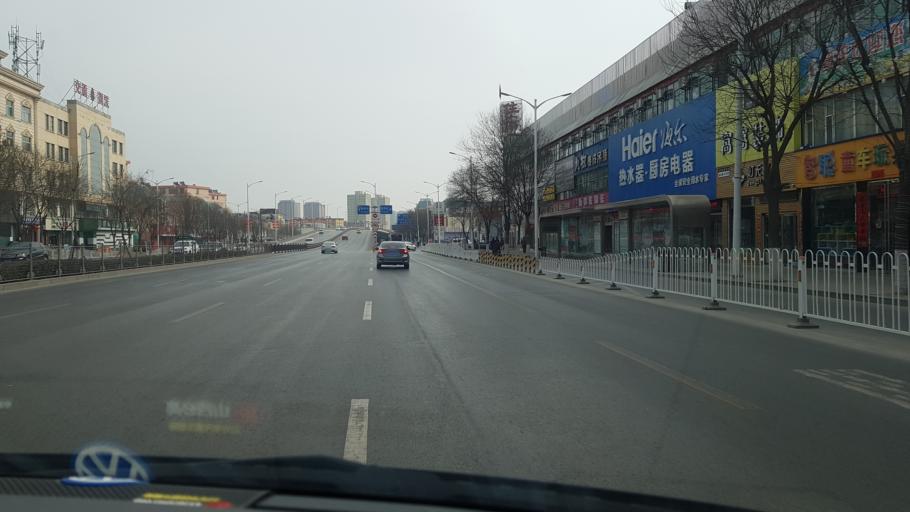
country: CN
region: Shanxi Sheng
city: Yuci
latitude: 37.6925
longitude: 112.7190
